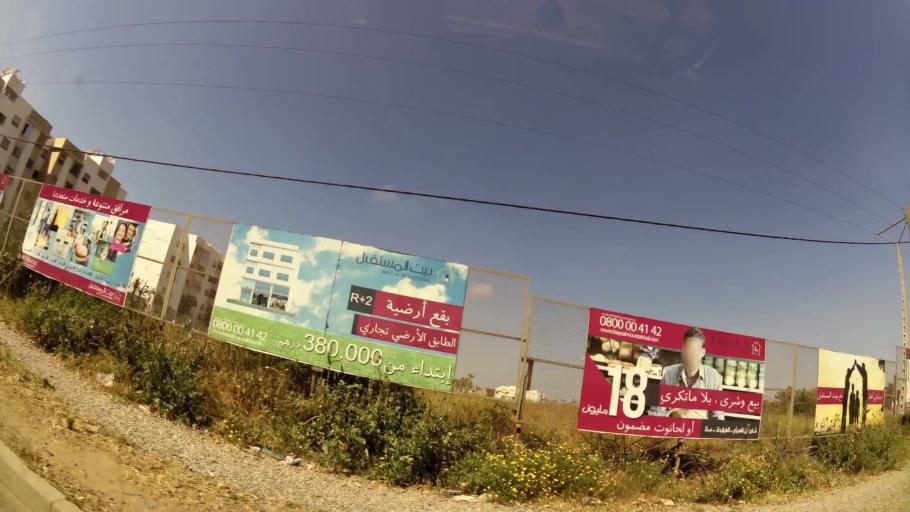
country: MA
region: Rabat-Sale-Zemmour-Zaer
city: Sale
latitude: 34.0788
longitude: -6.7531
